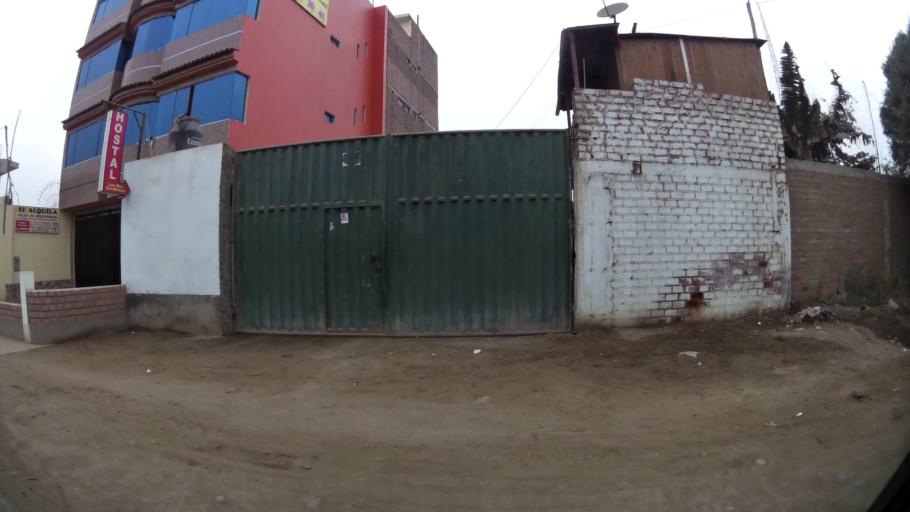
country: PE
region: Lima
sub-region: Lima
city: Urb. Santo Domingo
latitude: -11.8890
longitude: -77.0612
